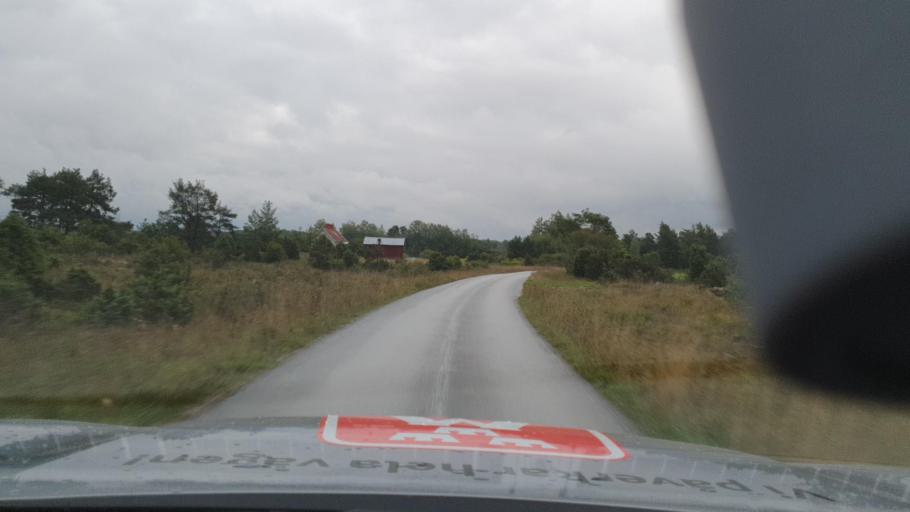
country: SE
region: Gotland
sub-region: Gotland
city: Slite
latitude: 57.8096
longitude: 18.5901
